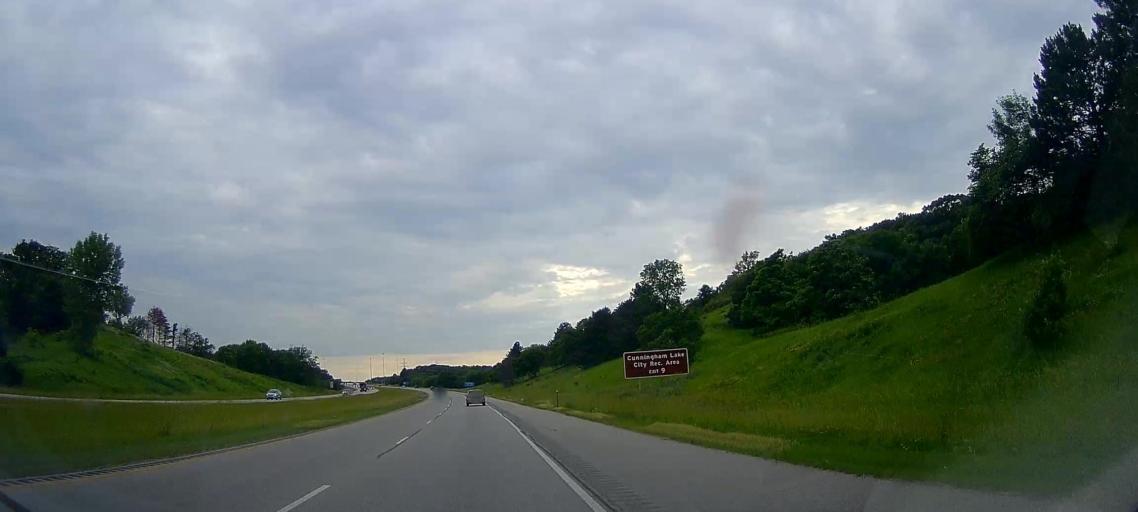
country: US
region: Iowa
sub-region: Pottawattamie County
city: Carter Lake
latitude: 41.3459
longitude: -96.0088
